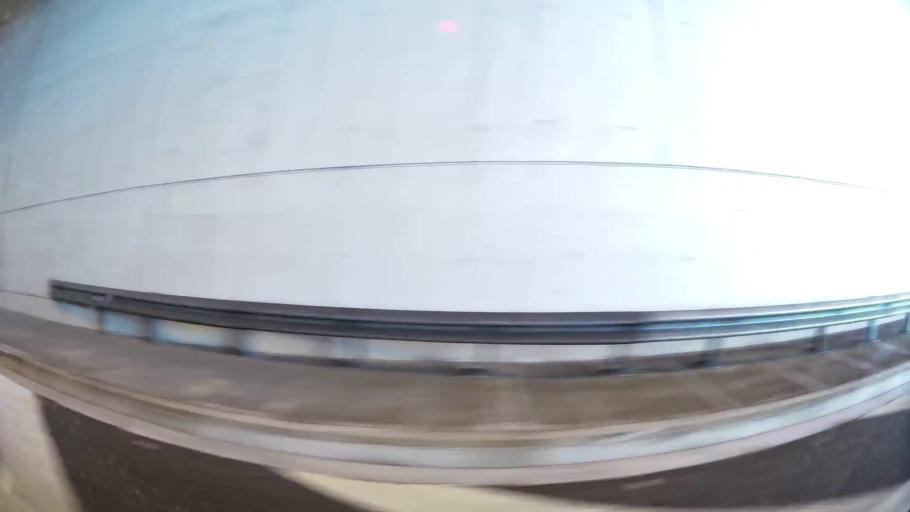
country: GR
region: Attica
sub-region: Nomarchia Athinas
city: Agia Paraskevi
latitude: 38.0080
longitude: 23.8369
